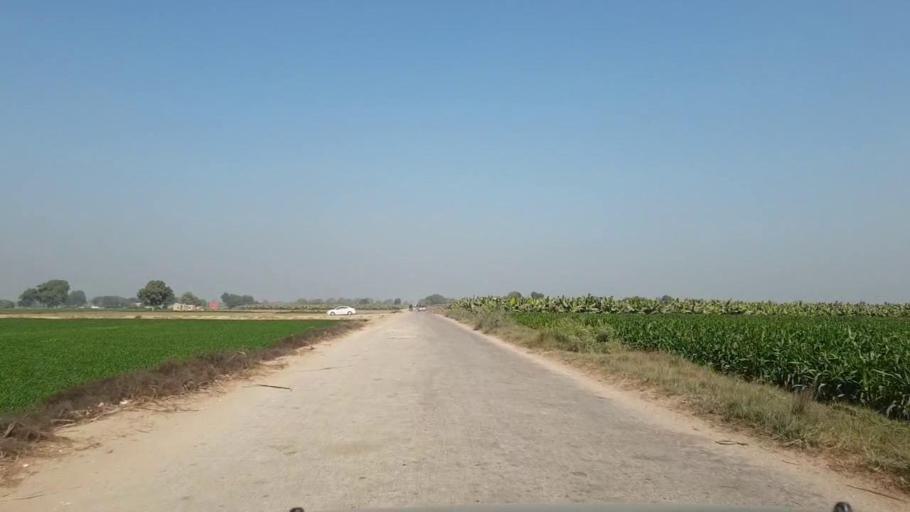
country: PK
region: Sindh
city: Matiari
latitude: 25.5896
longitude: 68.6010
